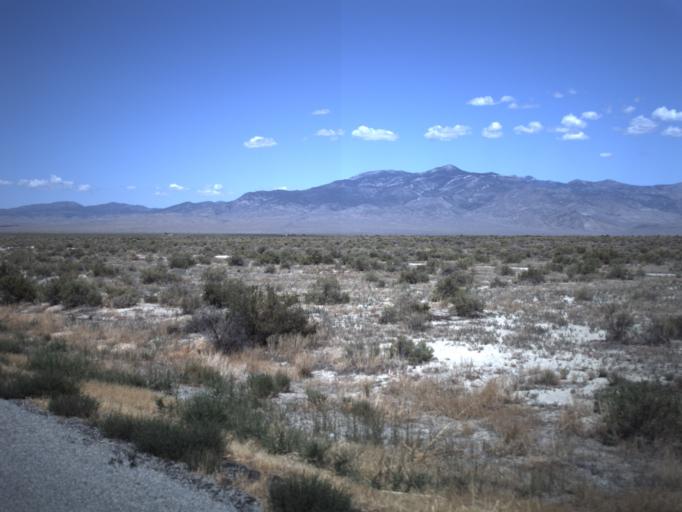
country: US
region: Nevada
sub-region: White Pine County
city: McGill
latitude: 39.0525
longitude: -113.9878
